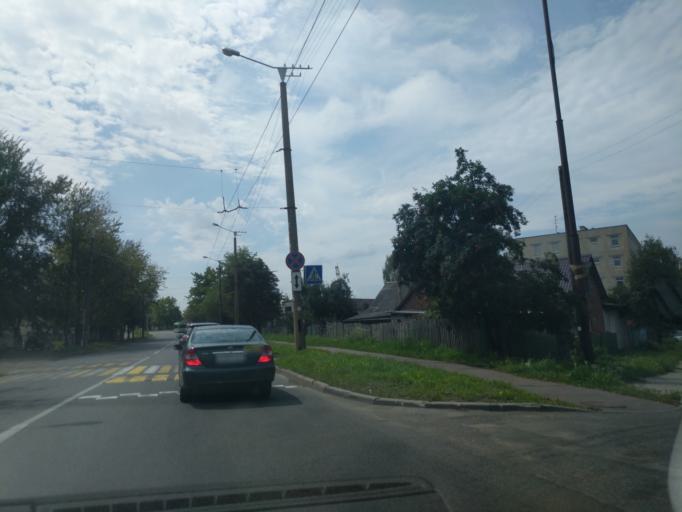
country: BY
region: Minsk
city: Novoye Medvezhino
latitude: 53.8911
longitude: 27.4831
